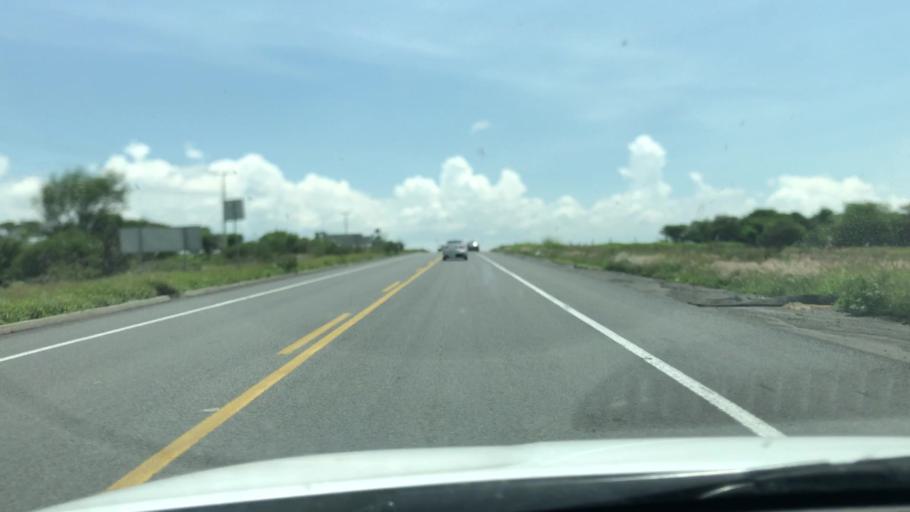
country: MX
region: Jalisco
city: Degollado
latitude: 20.3572
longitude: -102.1514
